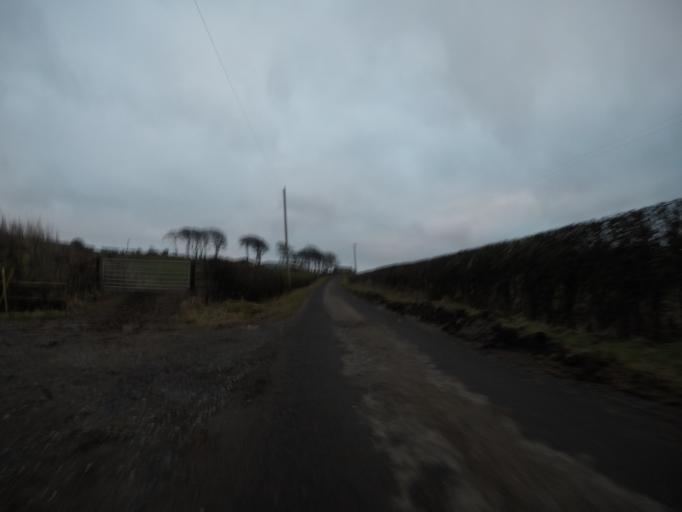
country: GB
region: Scotland
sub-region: North Ayrshire
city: Dalry
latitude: 55.6914
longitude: -4.7422
